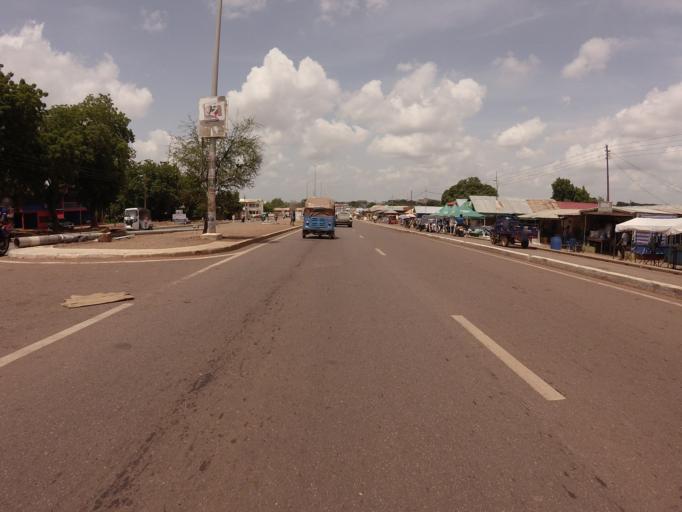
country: GH
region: Northern
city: Tamale
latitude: 9.3998
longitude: -0.8333
